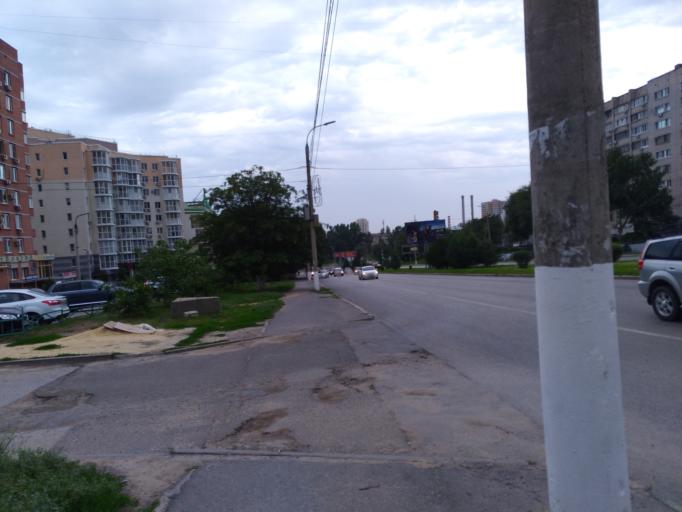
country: RU
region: Volgograd
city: Volgograd
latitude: 48.7260
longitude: 44.5252
